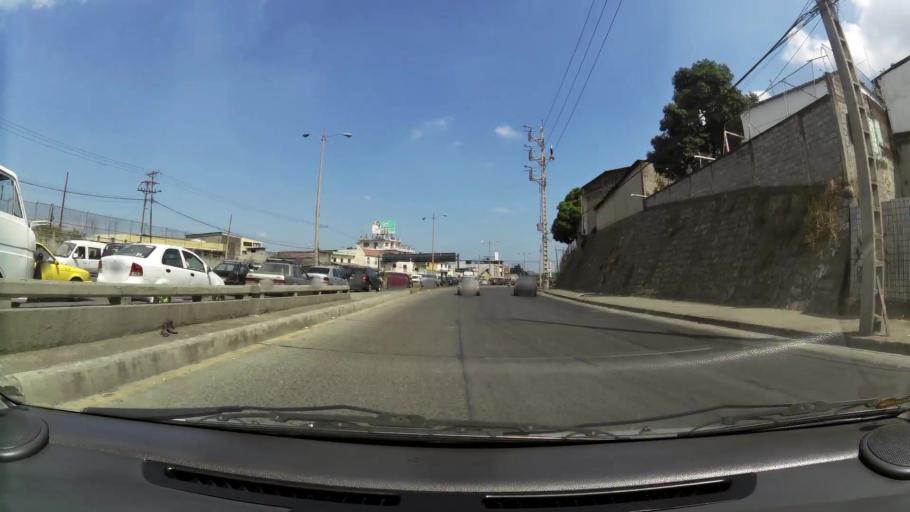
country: EC
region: Guayas
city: Guayaquil
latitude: -2.1241
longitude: -79.9311
